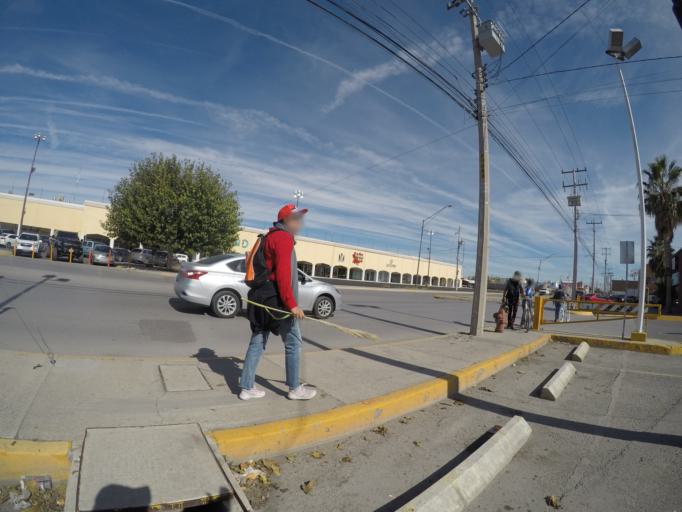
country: MX
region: Chihuahua
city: Ciudad Juarez
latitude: 31.7338
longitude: -106.4469
